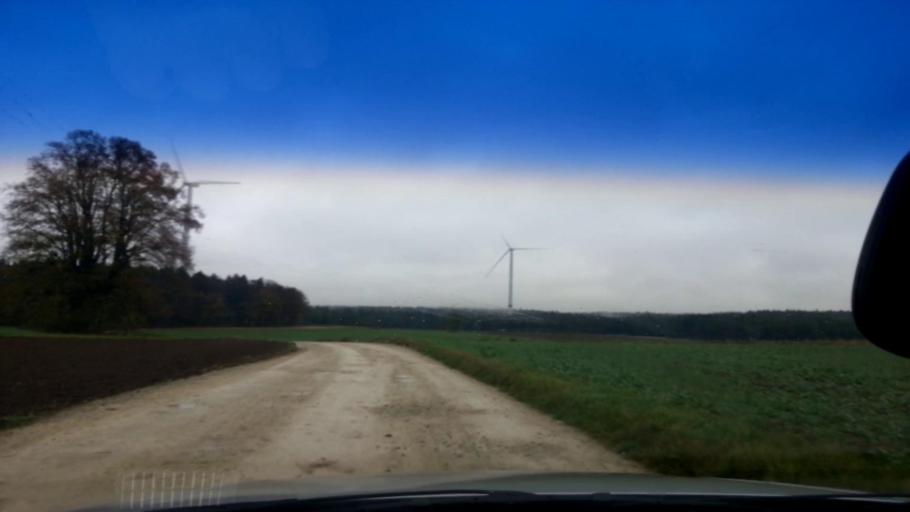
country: DE
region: Bavaria
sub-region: Upper Franconia
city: Wattendorf
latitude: 50.0086
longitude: 11.1476
